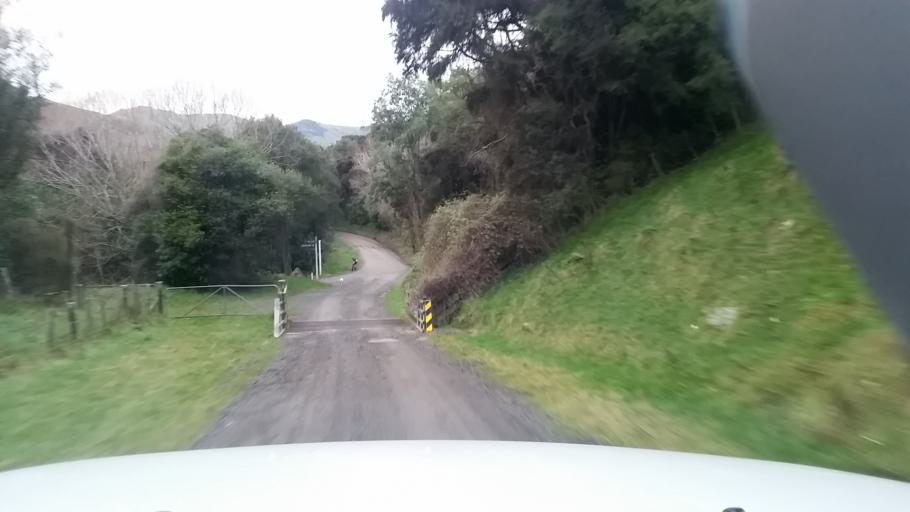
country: NZ
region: Canterbury
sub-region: Christchurch City
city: Christchurch
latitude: -43.7351
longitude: 172.7853
